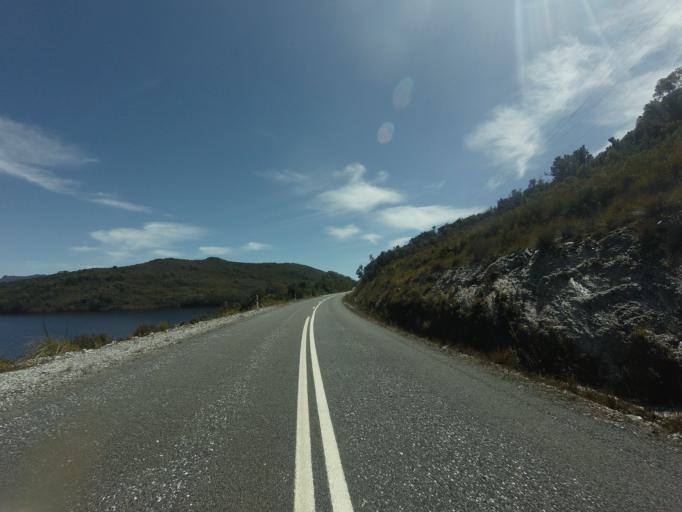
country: AU
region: Tasmania
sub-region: West Coast
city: Queenstown
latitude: -42.7970
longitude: 146.0720
